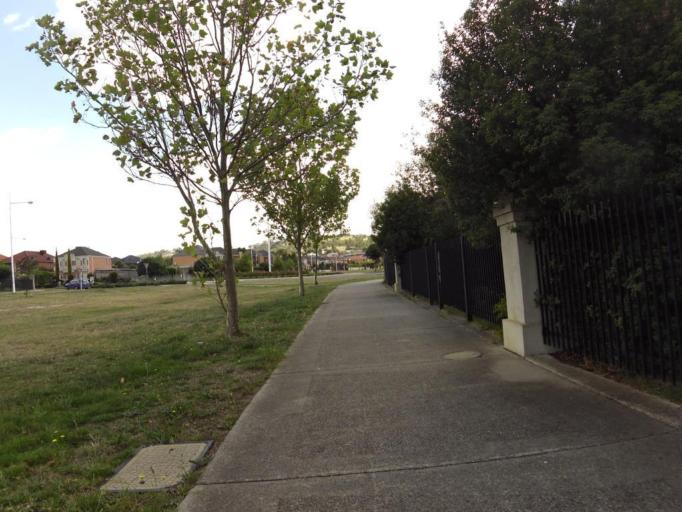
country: AU
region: Victoria
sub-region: Whittlesea
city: Mill Park
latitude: -37.6316
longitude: 145.0674
